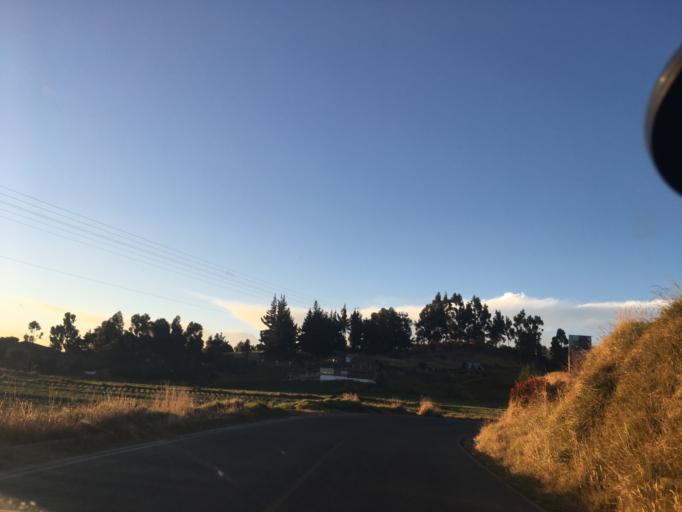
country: CO
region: Boyaca
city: Aquitania
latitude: 5.5604
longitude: -72.8808
